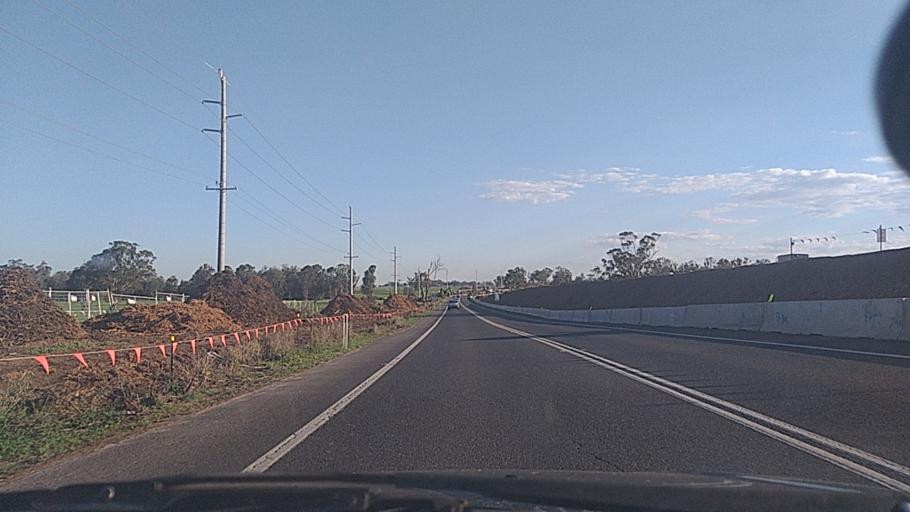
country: AU
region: New South Wales
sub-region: Liverpool
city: Bringelly
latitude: -33.9588
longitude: 150.7389
